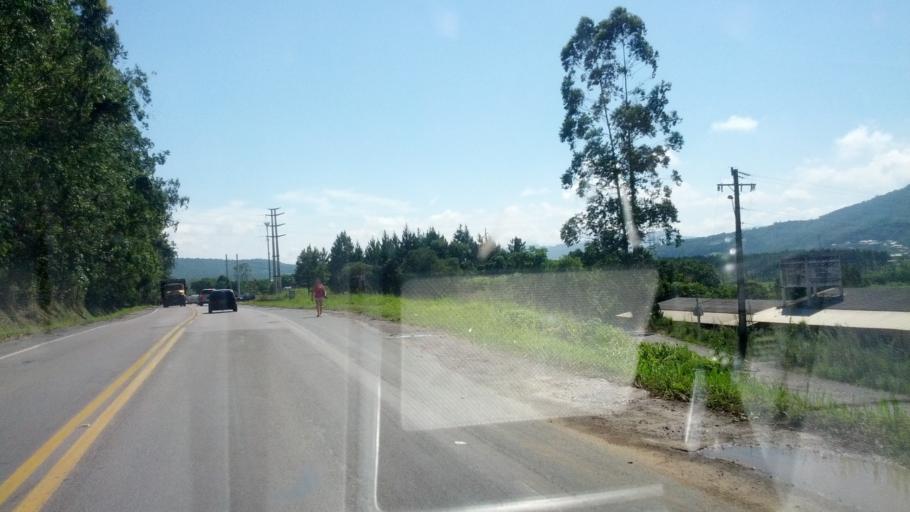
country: BR
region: Santa Catarina
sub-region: Rio Do Sul
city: Rio do Sul
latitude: -27.1862
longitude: -49.6065
